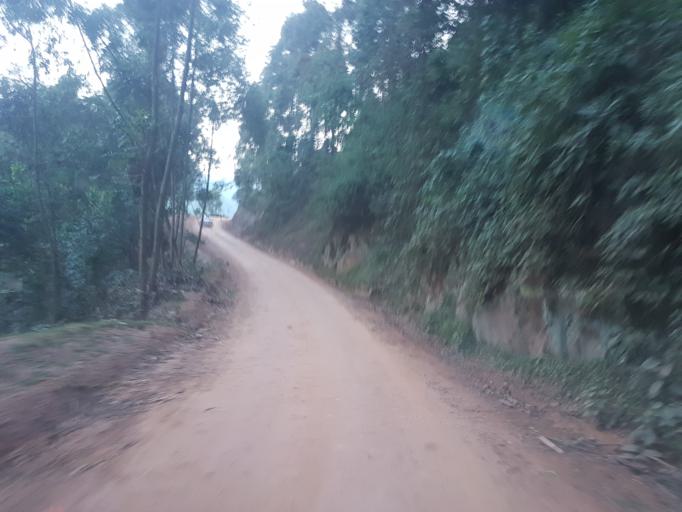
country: UG
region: Western Region
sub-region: Kanungu District
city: Kanungu
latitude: -0.9515
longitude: 29.8307
